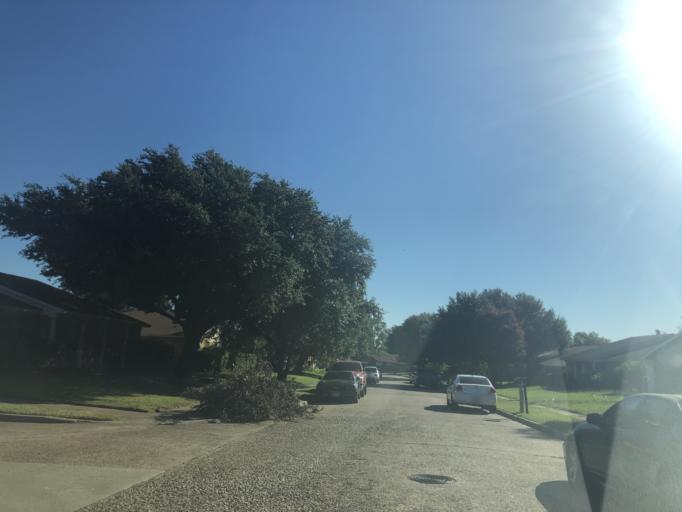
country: US
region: Texas
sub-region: Dallas County
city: Duncanville
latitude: 32.6406
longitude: -96.9523
